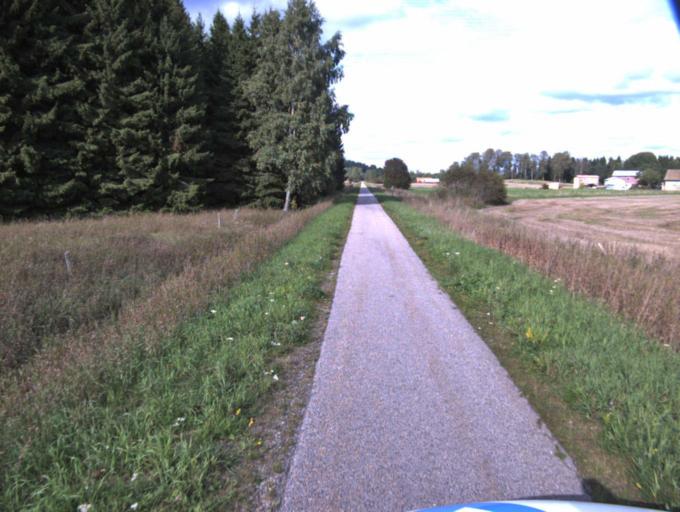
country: SE
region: Vaestra Goetaland
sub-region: Ulricehamns Kommun
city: Ulricehamn
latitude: 57.8793
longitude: 13.4297
